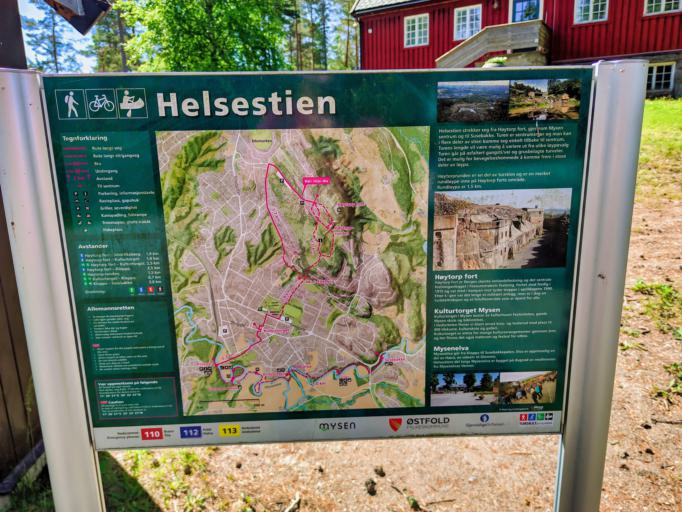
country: NO
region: Ostfold
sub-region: Eidsberg
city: Mysen
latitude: 59.5637
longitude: 11.3391
